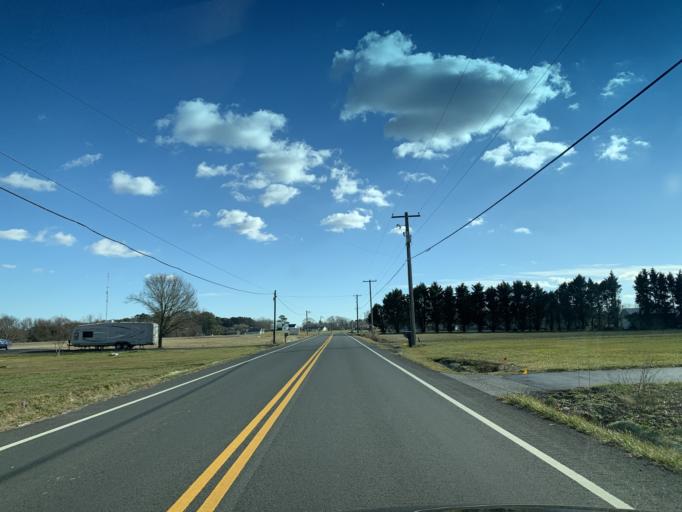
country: US
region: Maryland
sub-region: Worcester County
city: Berlin
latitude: 38.3525
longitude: -75.1944
